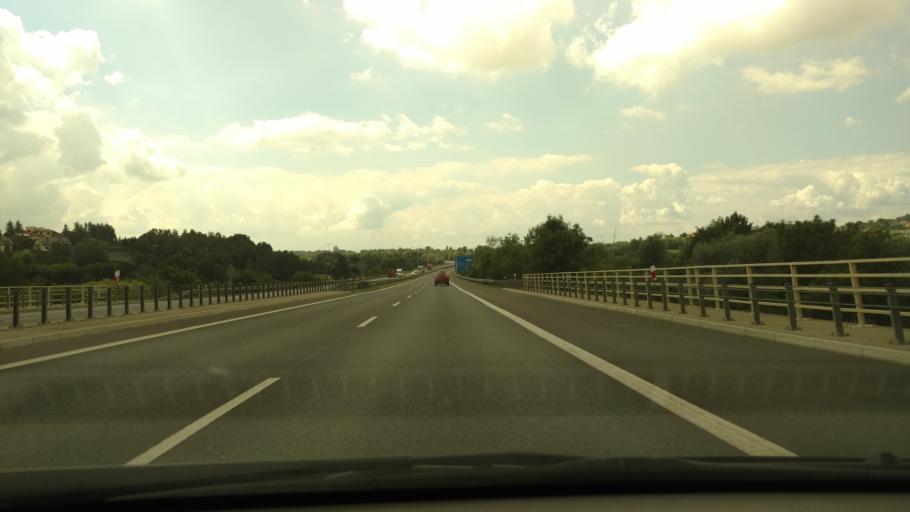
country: PL
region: Lesser Poland Voivodeship
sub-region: Powiat krakowski
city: Balice
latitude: 50.0932
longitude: 19.8158
